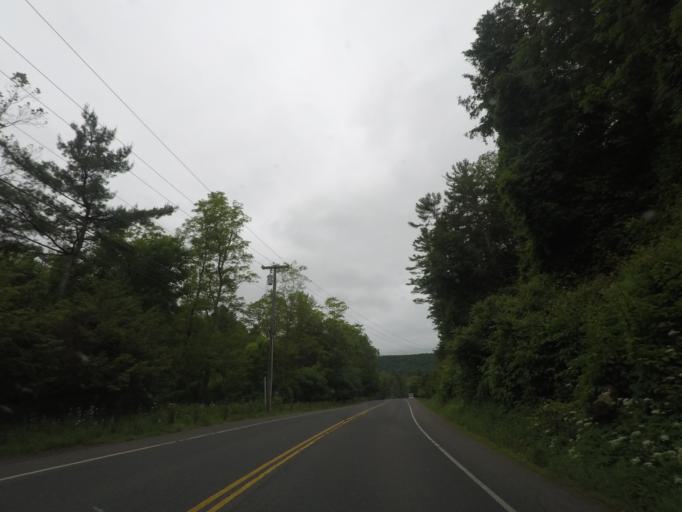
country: US
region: Connecticut
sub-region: Litchfield County
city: Canaan
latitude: 41.9363
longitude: -73.3923
